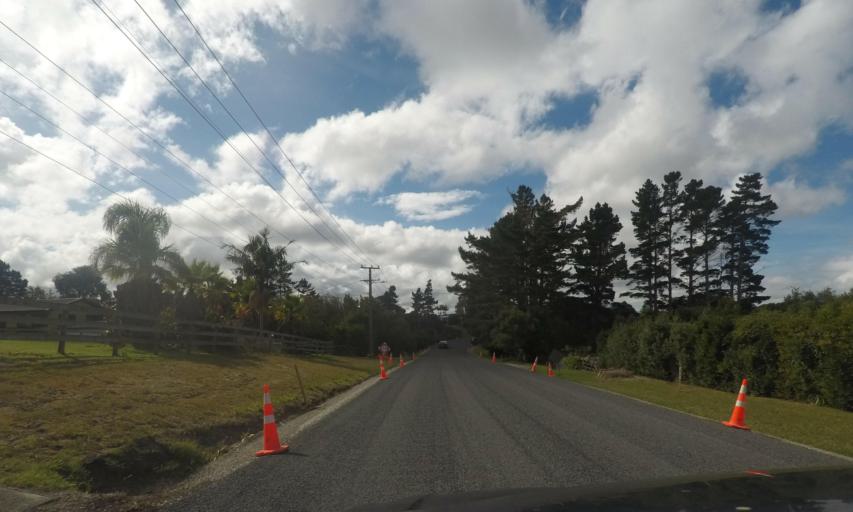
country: NZ
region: Auckland
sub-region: Auckland
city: Rosebank
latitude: -36.7912
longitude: 174.6369
